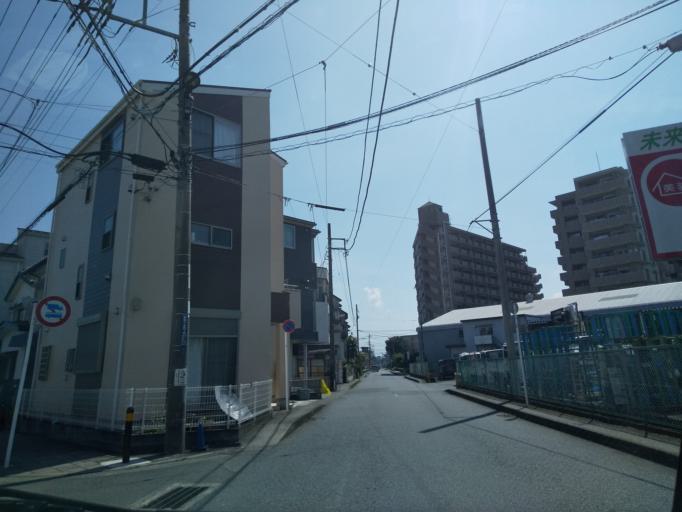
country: JP
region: Kanagawa
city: Minami-rinkan
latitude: 35.4764
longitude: 139.4331
